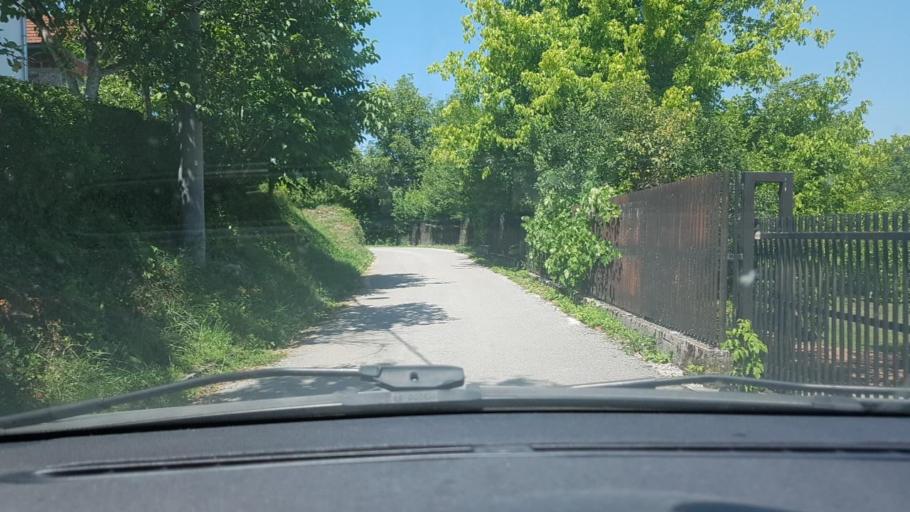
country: BA
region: Federation of Bosnia and Herzegovina
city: Orasac
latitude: 44.5601
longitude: 16.0855
